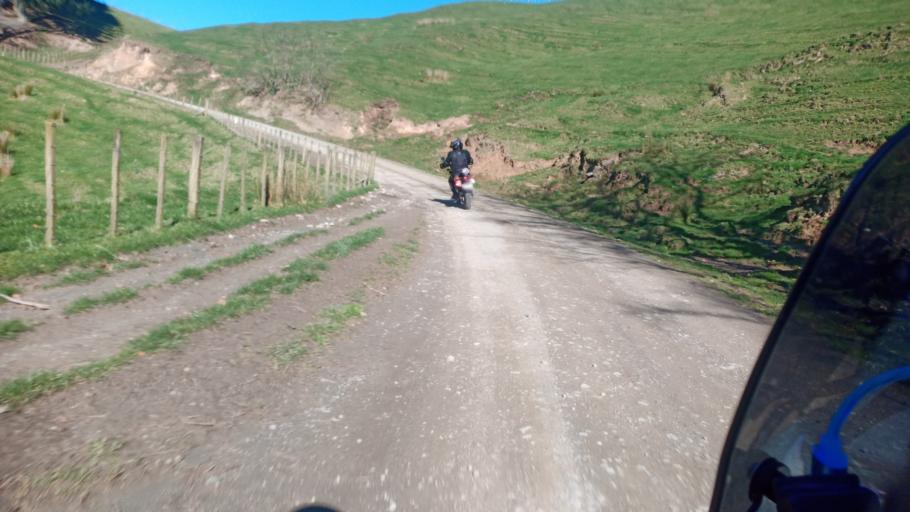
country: NZ
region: Gisborne
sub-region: Gisborne District
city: Gisborne
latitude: -38.2906
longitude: 177.8730
